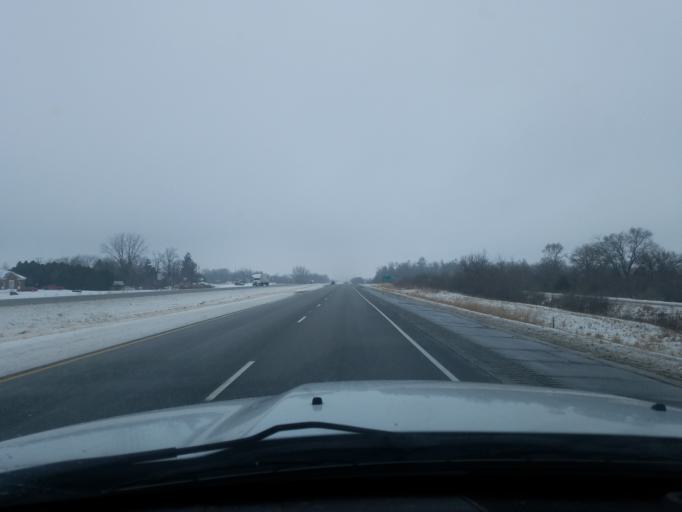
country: US
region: Indiana
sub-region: Fulton County
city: Rochester
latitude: 40.9575
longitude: -86.1682
